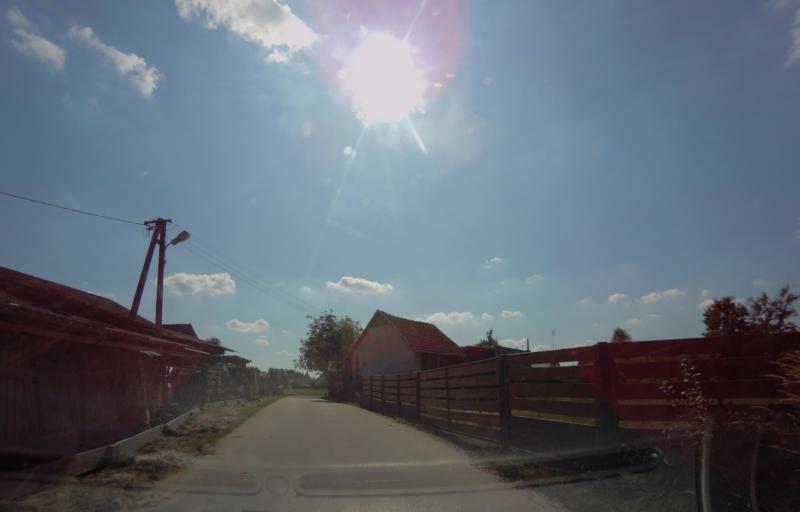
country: PL
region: Subcarpathian Voivodeship
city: Nowa Sarzyna
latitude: 50.3134
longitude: 22.3369
